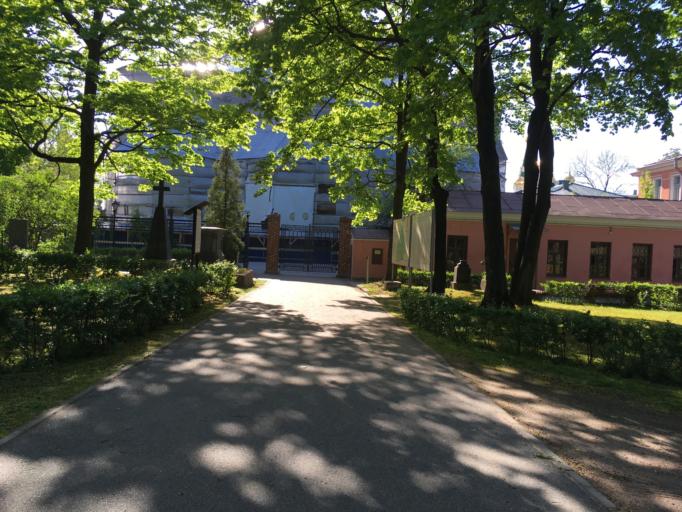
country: RU
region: St.-Petersburg
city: Admiralteisky
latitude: 59.8987
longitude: 30.3233
